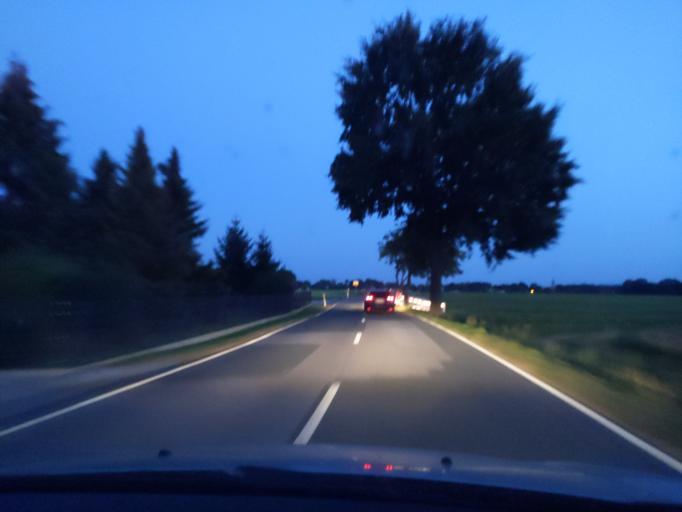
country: DE
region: Saxony
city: Malschwitz
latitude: 51.2747
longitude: 14.5178
